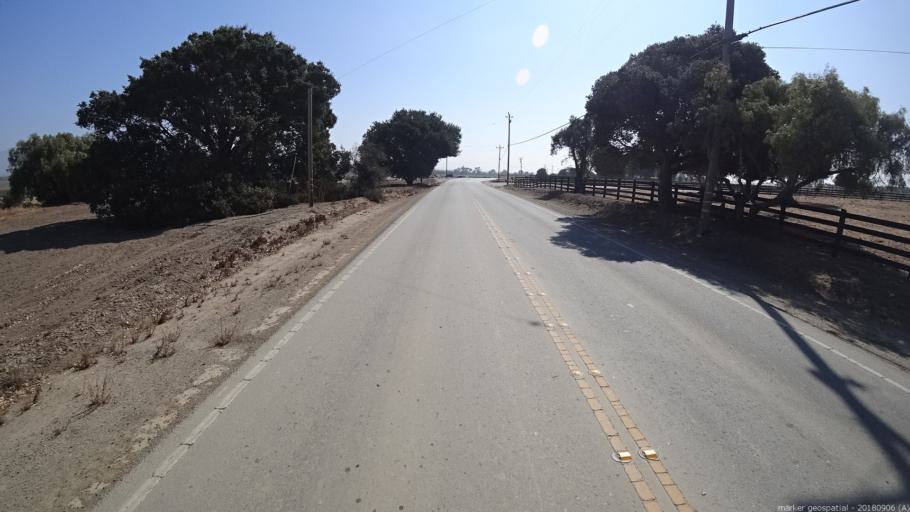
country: US
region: California
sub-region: Monterey County
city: Chualar
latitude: 36.5625
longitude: -121.5600
